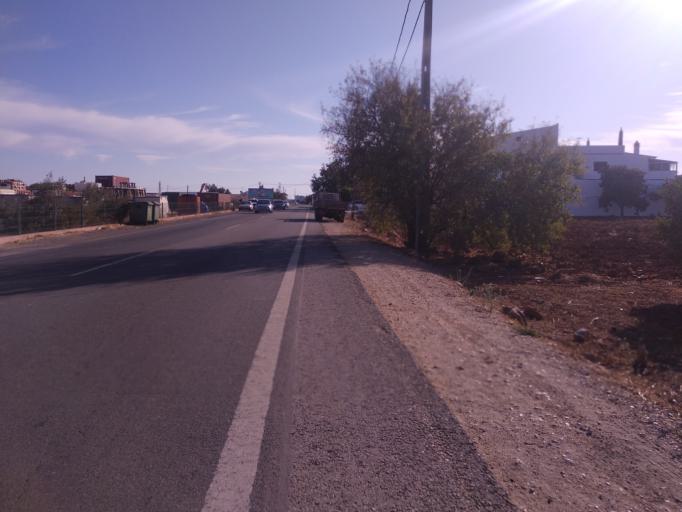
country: PT
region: Faro
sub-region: Faro
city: Faro
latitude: 37.0728
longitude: -7.9175
